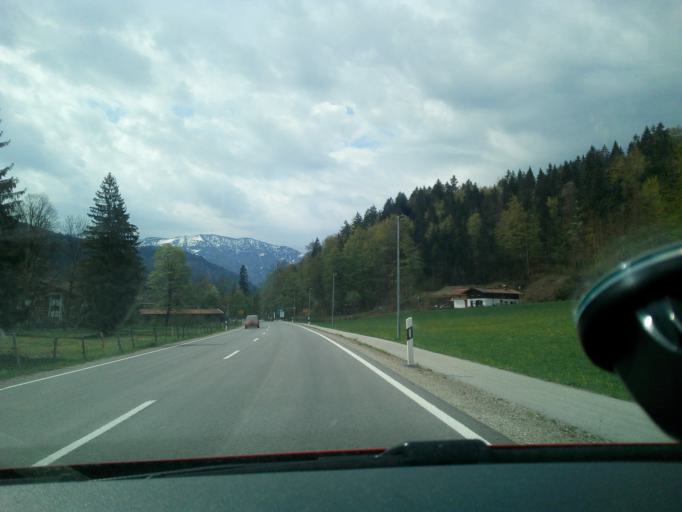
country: DE
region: Bavaria
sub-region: Upper Bavaria
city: Kreuth
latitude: 47.6493
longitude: 11.7464
